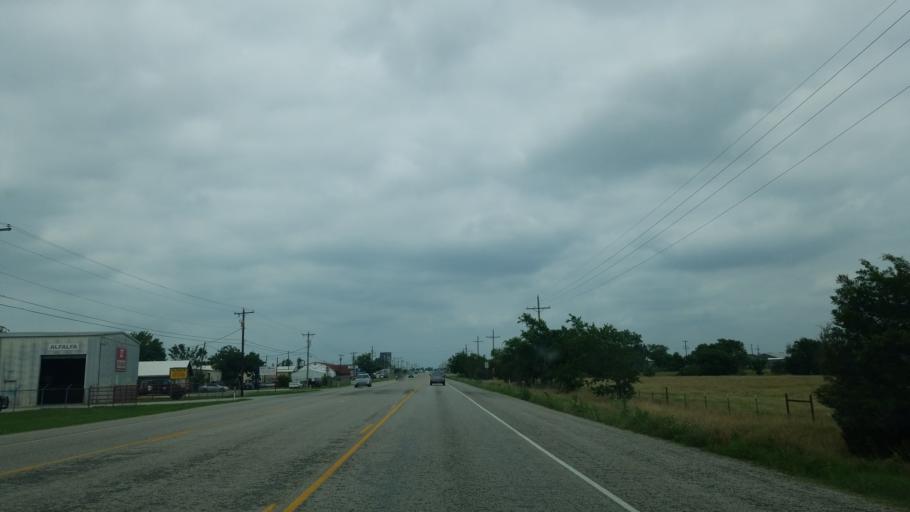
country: US
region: Texas
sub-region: Denton County
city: Pilot Point
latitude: 33.4010
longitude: -96.9441
